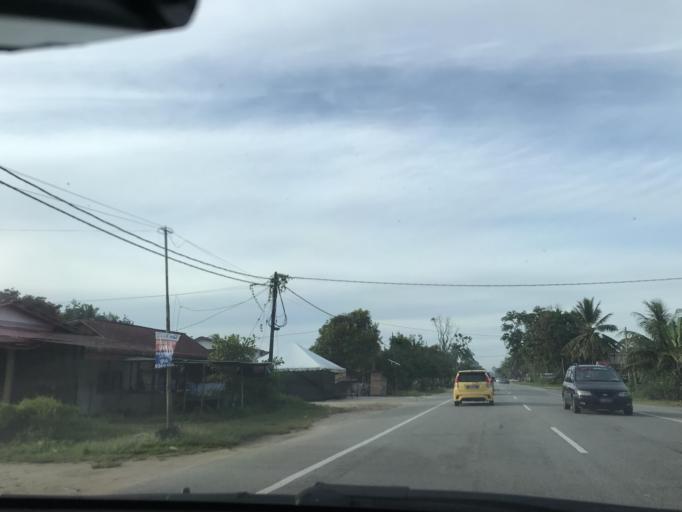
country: MY
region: Kelantan
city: Ketereh
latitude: 5.9809
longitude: 102.1902
